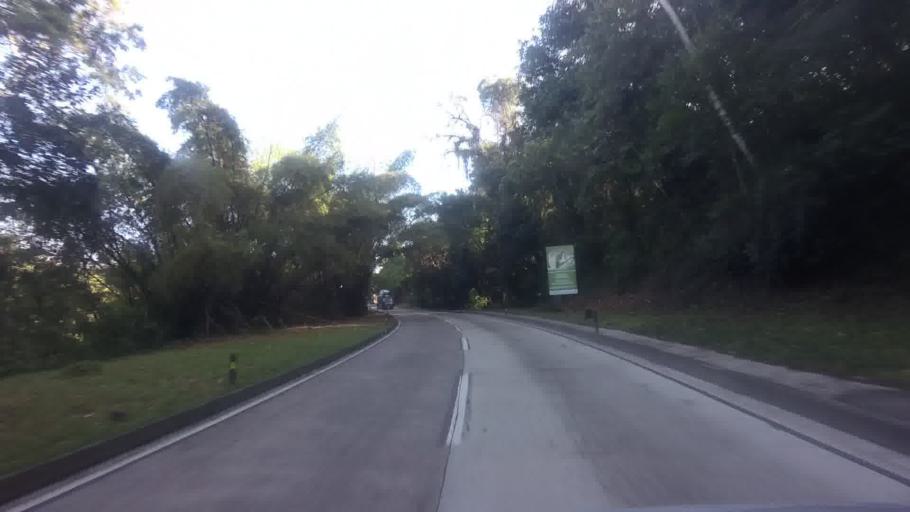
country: BR
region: Rio de Janeiro
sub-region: Petropolis
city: Petropolis
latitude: -22.5970
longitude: -43.2790
